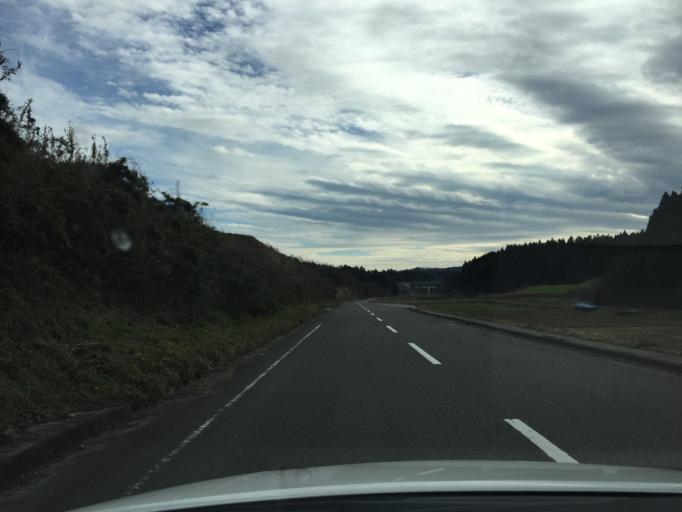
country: JP
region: Fukushima
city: Funehikimachi-funehiki
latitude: 37.3002
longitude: 140.6017
